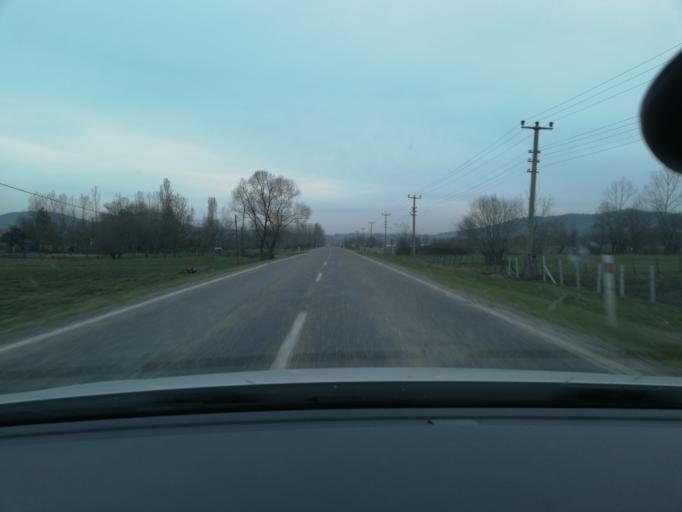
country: TR
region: Zonguldak
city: Saltukova
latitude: 41.5067
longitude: 32.1001
